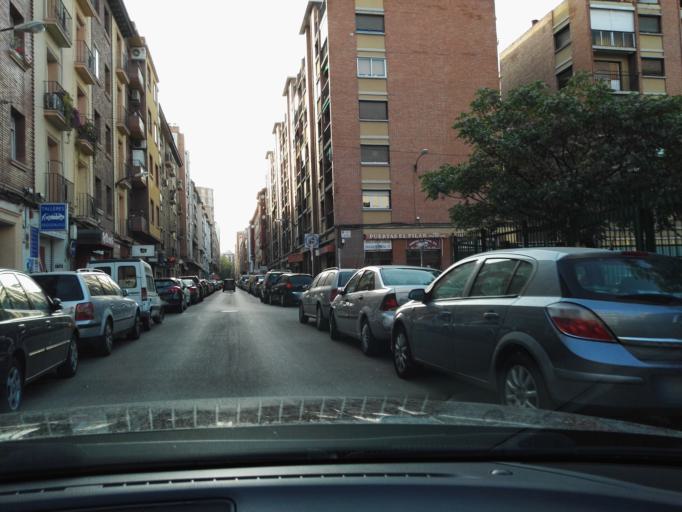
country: ES
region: Aragon
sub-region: Provincia de Zaragoza
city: Zaragoza
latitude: 41.6375
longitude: -0.8775
